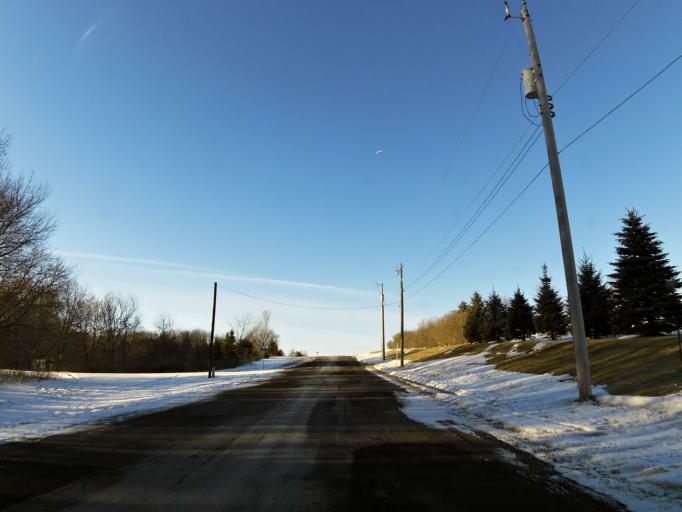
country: US
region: Minnesota
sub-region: Dakota County
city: Hastings
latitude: 44.7960
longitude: -92.8661
